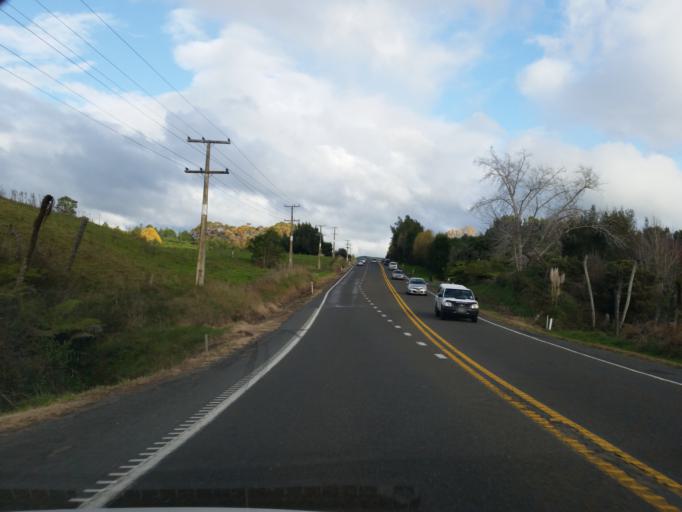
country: NZ
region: Bay of Plenty
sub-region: Tauranga City
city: Tauranga
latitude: -37.6722
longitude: 176.0222
